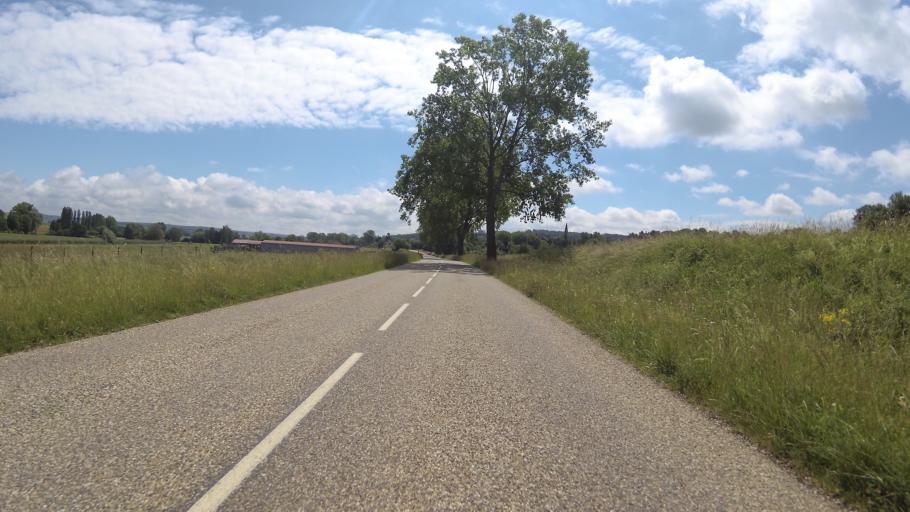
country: FR
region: Alsace
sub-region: Departement du Bas-Rhin
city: Diemeringen
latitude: 48.9561
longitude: 7.1483
